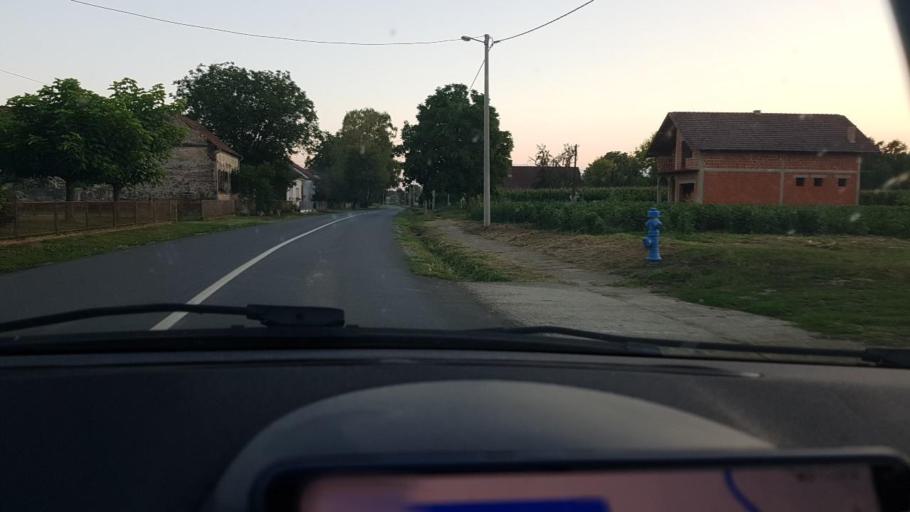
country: HR
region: Bjelovarsko-Bilogorska
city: Zdralovi
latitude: 45.8488
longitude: 16.9762
